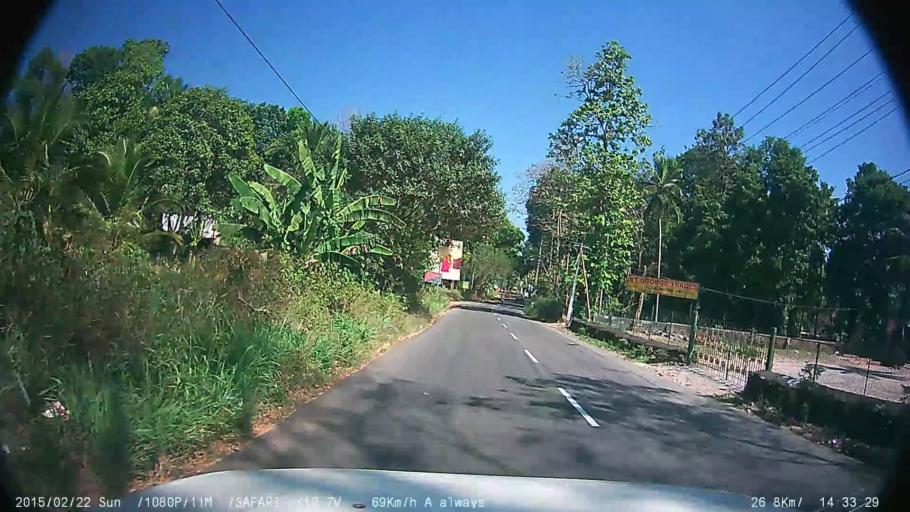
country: IN
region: Kerala
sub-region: Kottayam
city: Erattupetta
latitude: 9.5631
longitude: 76.7693
